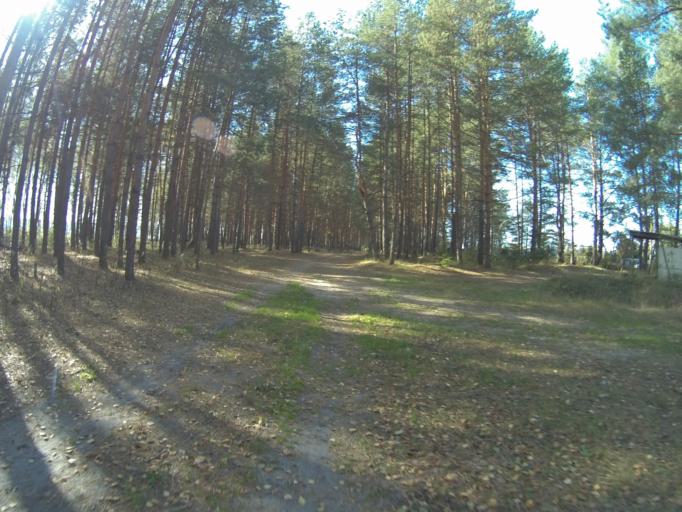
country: RU
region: Vladimir
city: Raduzhnyy
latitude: 56.0331
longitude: 40.3521
